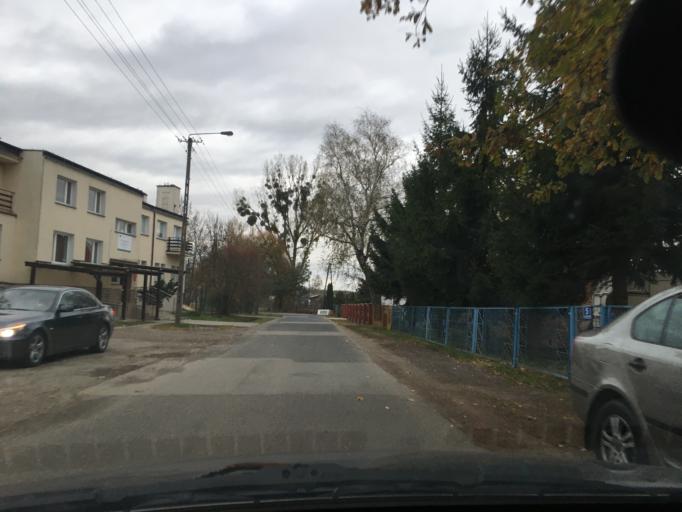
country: PL
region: Lodz Voivodeship
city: Zabia Wola
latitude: 52.0318
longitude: 20.6923
